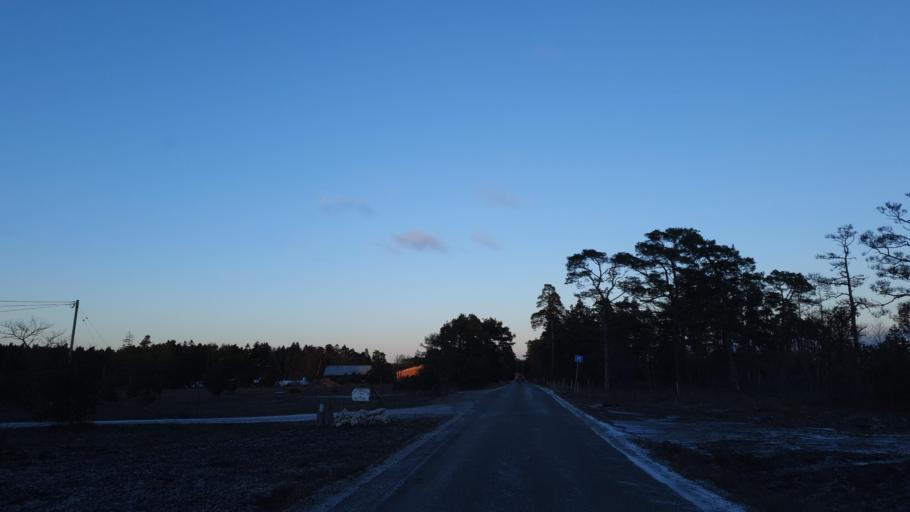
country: SE
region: Gotland
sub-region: Gotland
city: Slite
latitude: 57.3794
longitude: 18.8046
